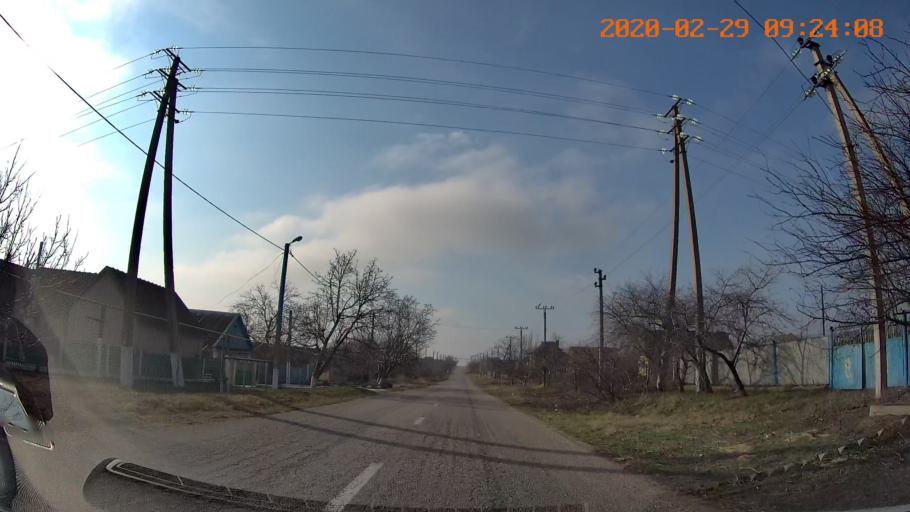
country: MD
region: Telenesti
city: Pervomaisc
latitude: 46.7192
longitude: 29.9594
